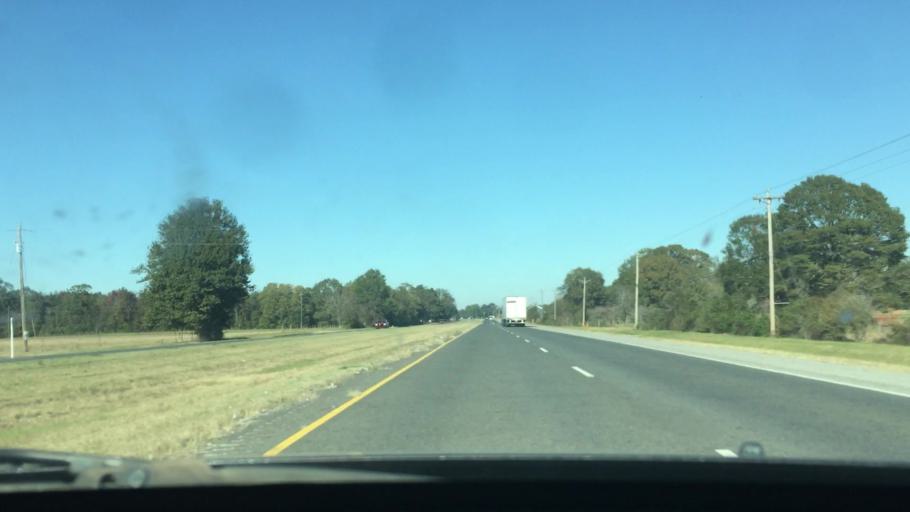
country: US
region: Louisiana
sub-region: Richland Parish
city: Rayville
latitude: 32.3663
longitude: -91.7728
